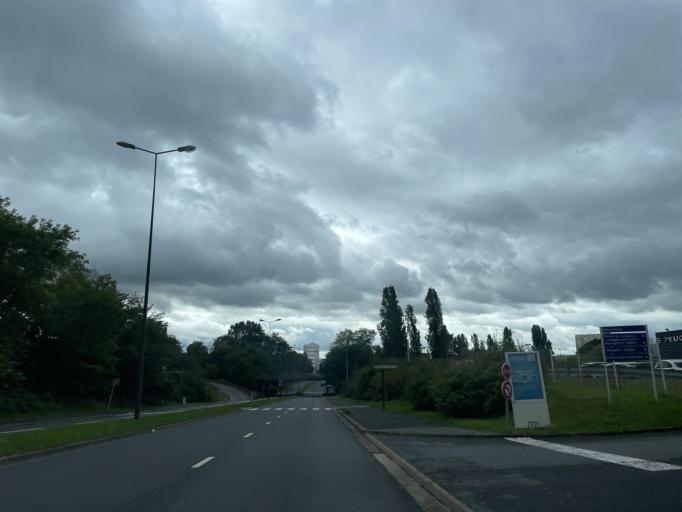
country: FR
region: Ile-de-France
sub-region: Departement de Seine-et-Marne
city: Fublaines
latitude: 48.9584
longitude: 2.9113
